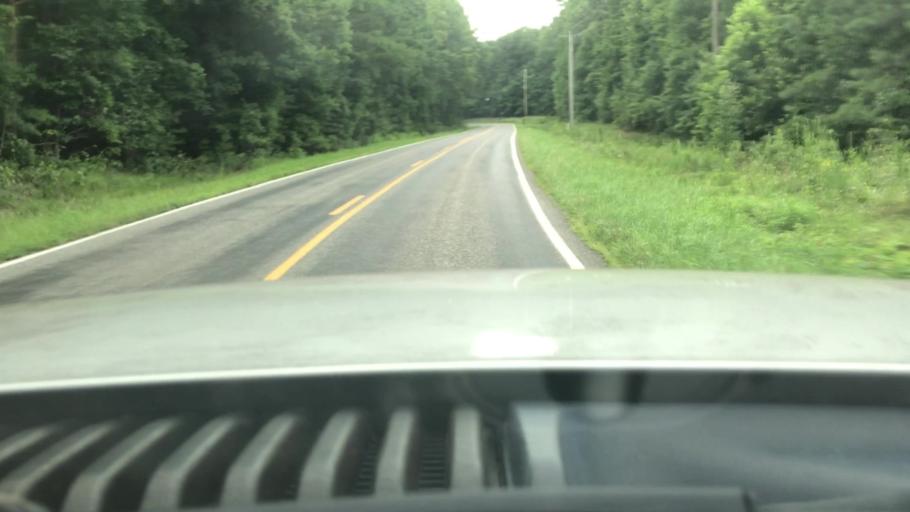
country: US
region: North Carolina
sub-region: Surry County
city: Dobson
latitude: 36.4105
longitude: -80.8169
